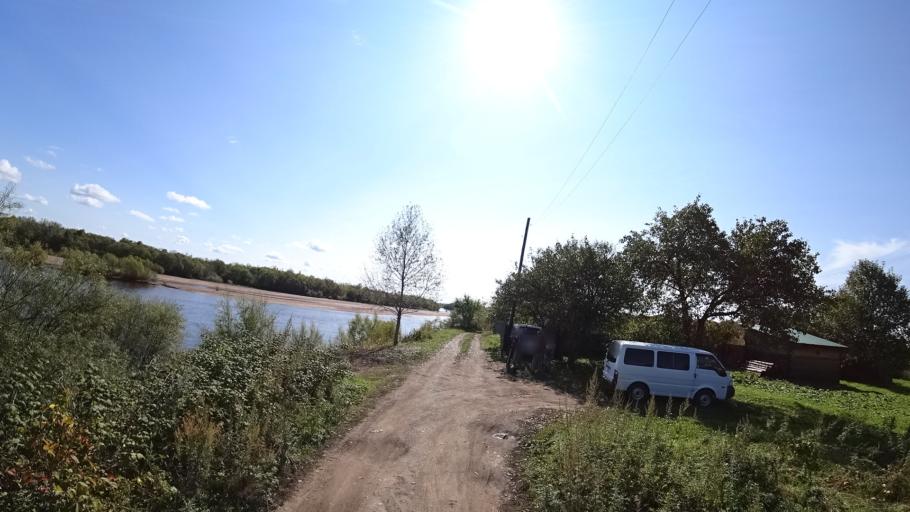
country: RU
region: Amur
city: Arkhara
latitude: 49.3990
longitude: 130.1305
